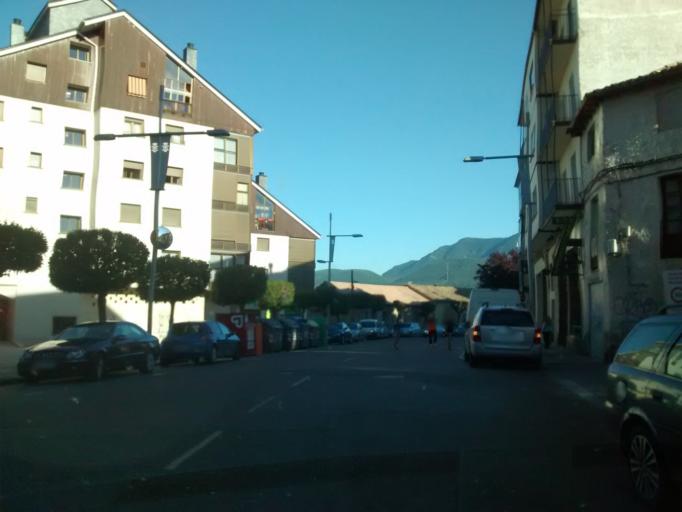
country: ES
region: Aragon
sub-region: Provincia de Huesca
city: Jaca
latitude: 42.5706
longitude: -0.5467
